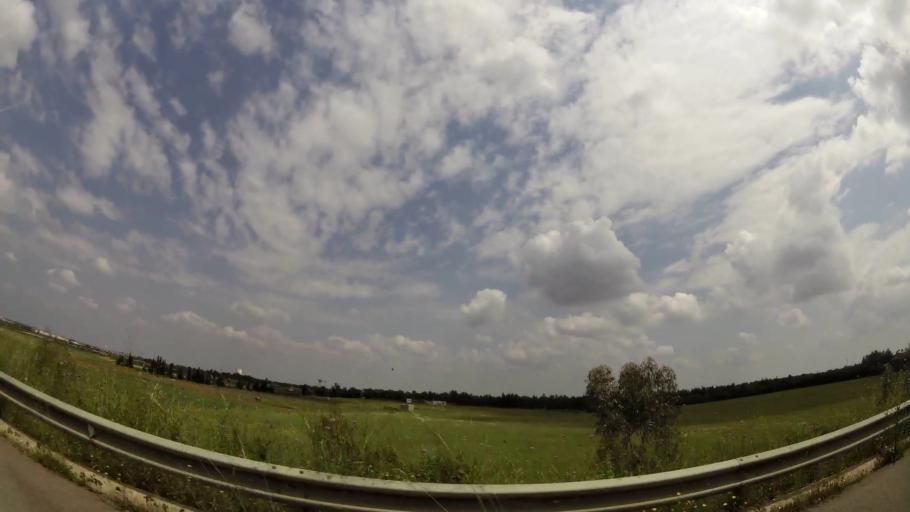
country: MA
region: Rabat-Sale-Zemmour-Zaer
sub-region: Khemisset
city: Tiflet
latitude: 33.9771
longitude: -6.5144
